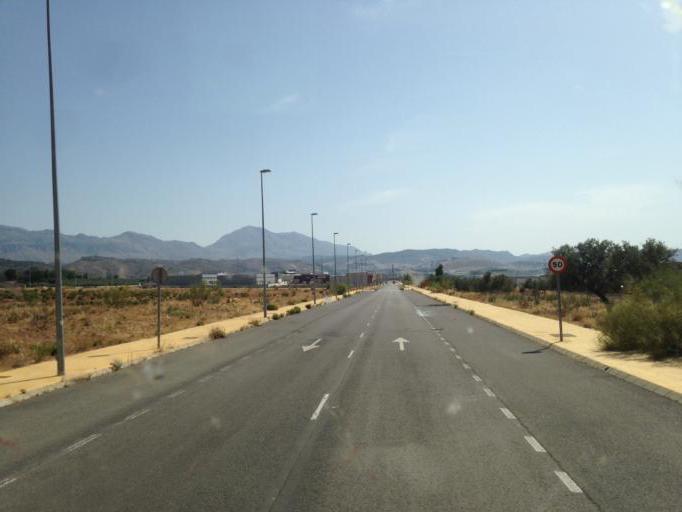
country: ES
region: Andalusia
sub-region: Provincia de Malaga
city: Antequera
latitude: 37.0437
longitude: -4.5168
